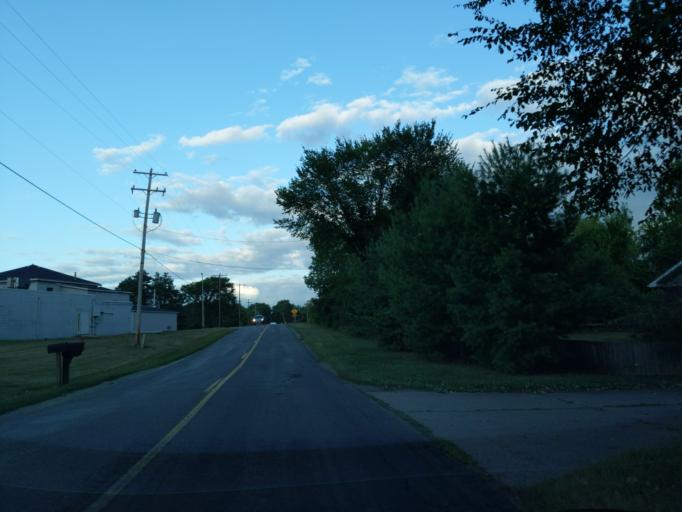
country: US
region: Michigan
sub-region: Ingham County
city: Holt
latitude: 42.6111
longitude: -84.4940
